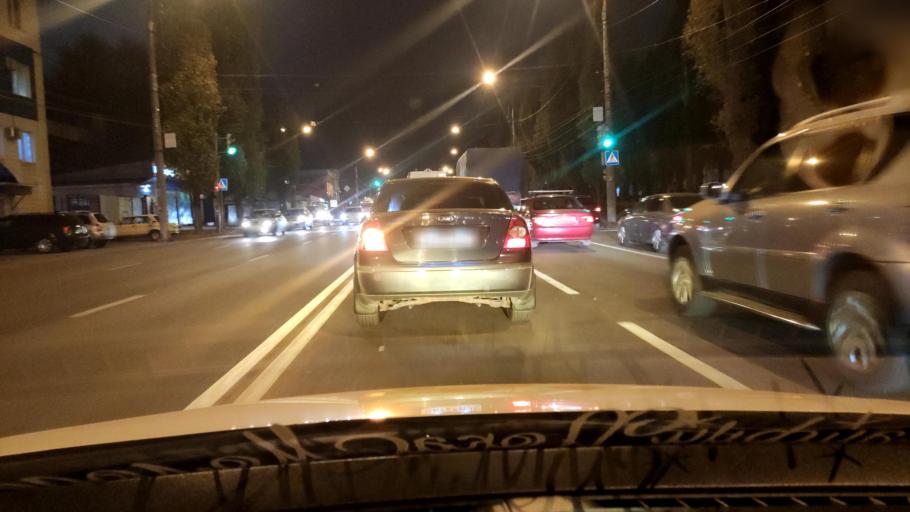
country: RU
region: Voronezj
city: Voronezh
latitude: 51.6884
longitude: 39.1653
